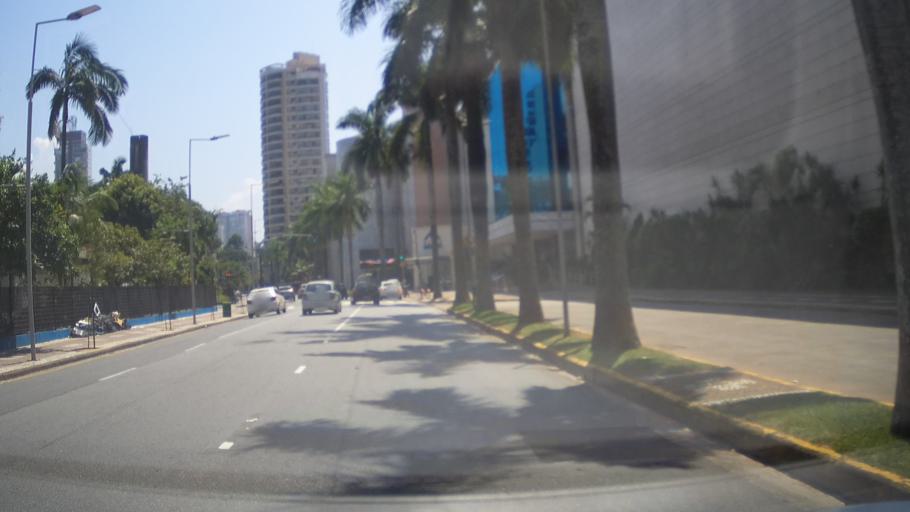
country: BR
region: Sao Paulo
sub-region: Santos
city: Santos
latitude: -23.9780
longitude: -46.3092
